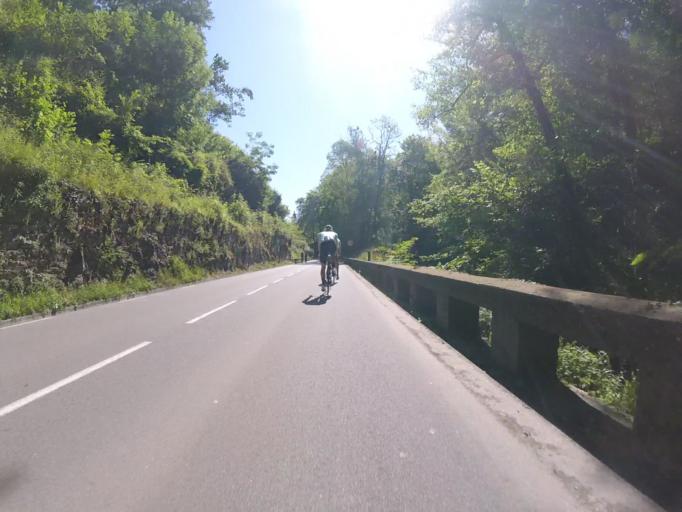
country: ES
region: Basque Country
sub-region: Provincia de Guipuzcoa
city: Alegria de Oria
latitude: 43.1231
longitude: -2.1003
